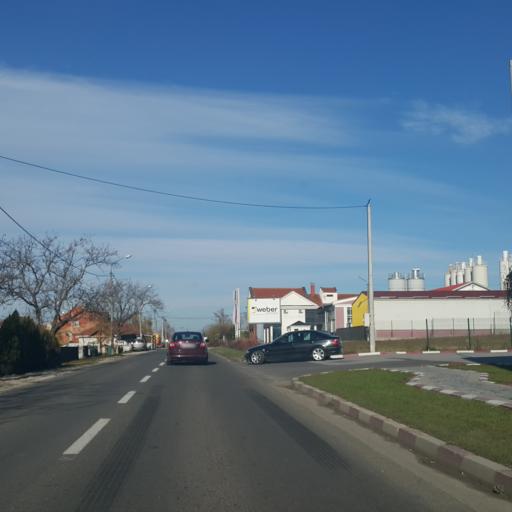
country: RS
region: Central Serbia
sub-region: Sumadijski Okrug
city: Topola
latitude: 44.2620
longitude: 20.6856
